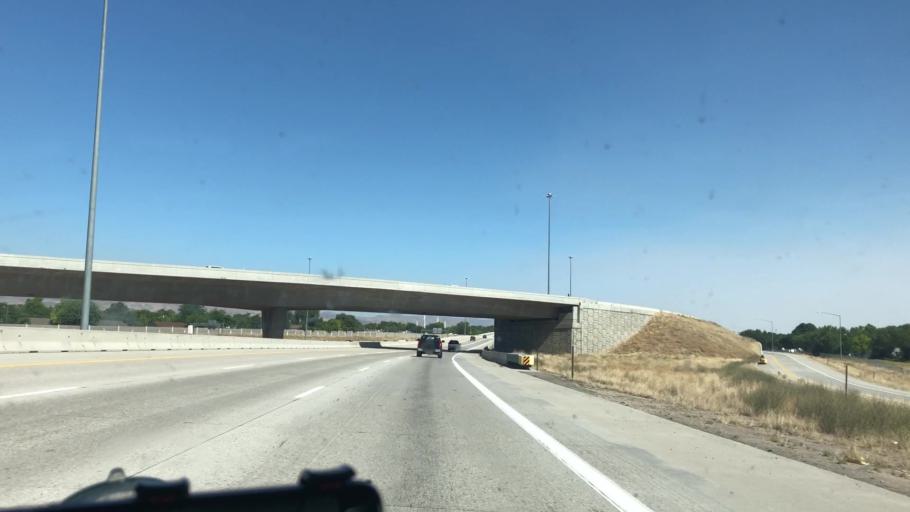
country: US
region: Idaho
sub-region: Ada County
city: Garden City
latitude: 43.5966
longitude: -116.2908
